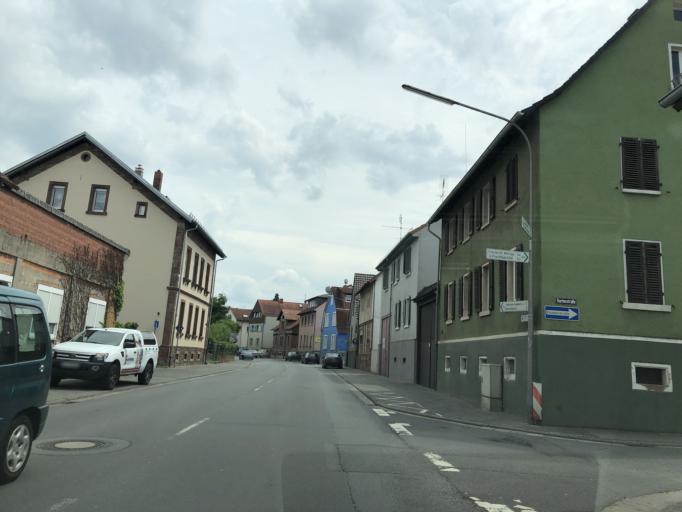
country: DE
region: Hesse
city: Gross-Bieberau
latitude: 49.7997
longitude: 8.8297
